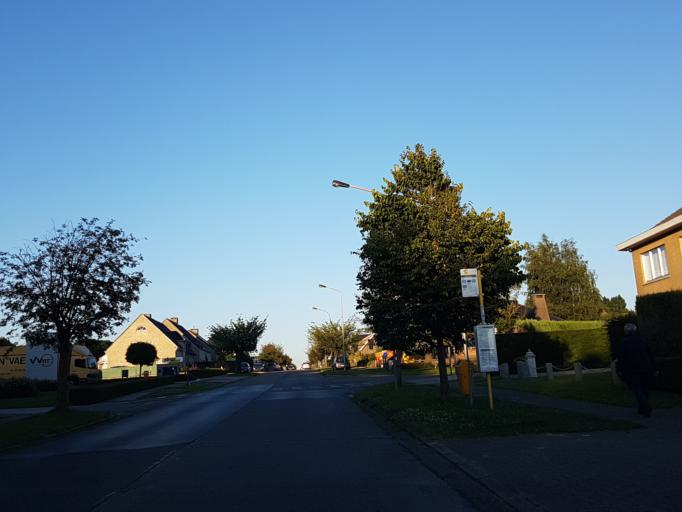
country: BE
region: Flanders
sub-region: Provincie Vlaams-Brabant
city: Dilbeek
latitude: 50.8658
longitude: 4.2540
